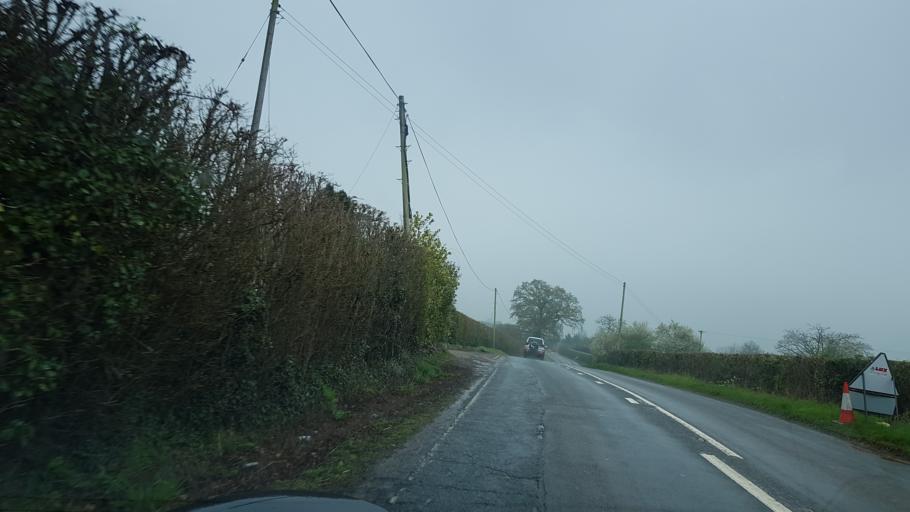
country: GB
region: England
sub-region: Herefordshire
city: Bromyard
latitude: 52.1594
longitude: -2.5368
